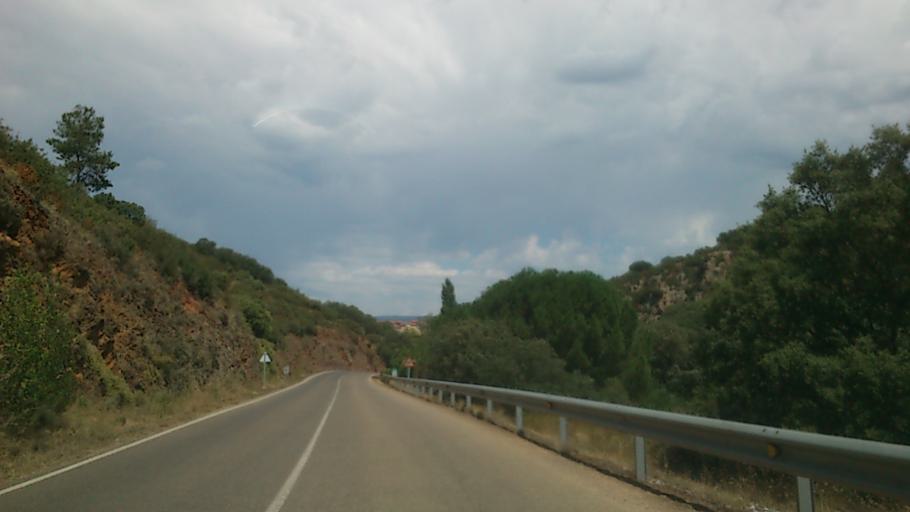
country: ES
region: Castille and Leon
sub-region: Provincia de Burgos
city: Frias
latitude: 42.7536
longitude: -3.2970
